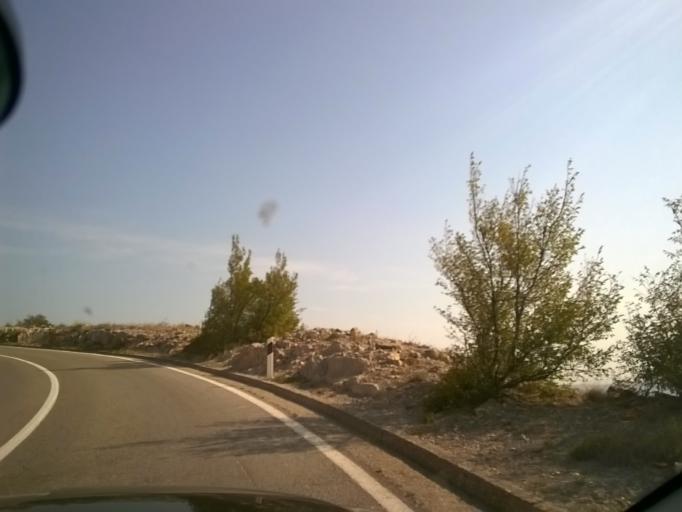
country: HR
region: Licko-Senjska
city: Karlobag
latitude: 44.5134
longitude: 15.1129
